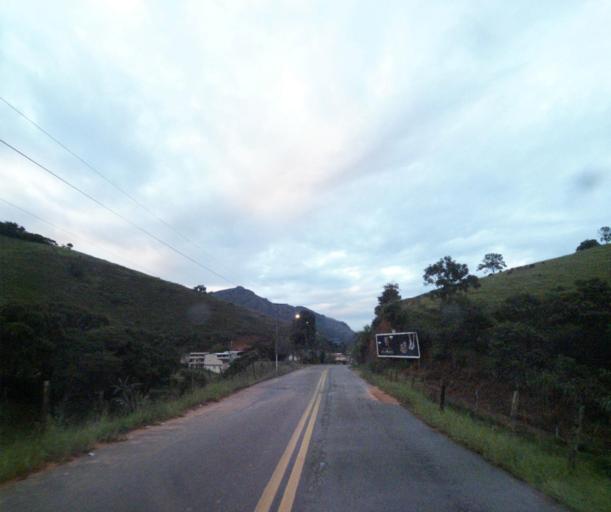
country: BR
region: Espirito Santo
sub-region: Muniz Freire
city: Muniz Freire
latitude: -20.4724
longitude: -41.4158
